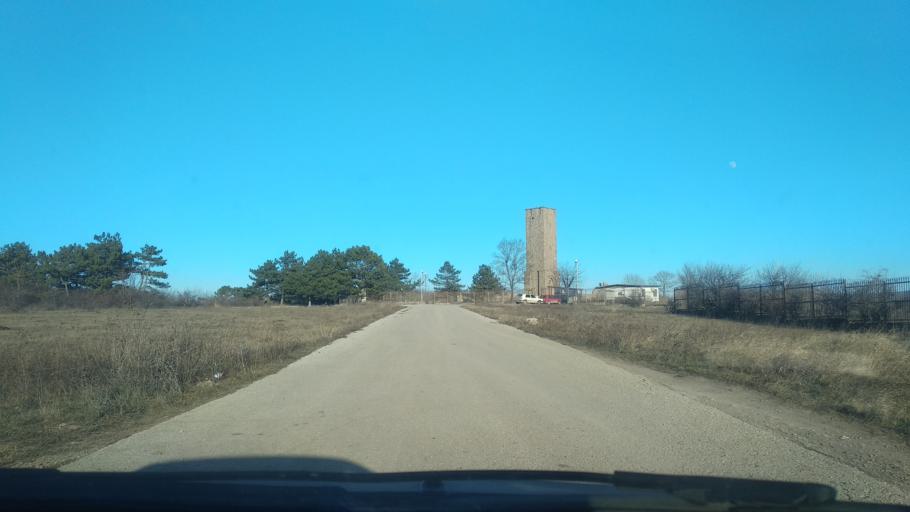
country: XK
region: Pristina
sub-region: Kosovo Polje
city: Kosovo Polje
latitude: 42.6898
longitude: 21.1215
